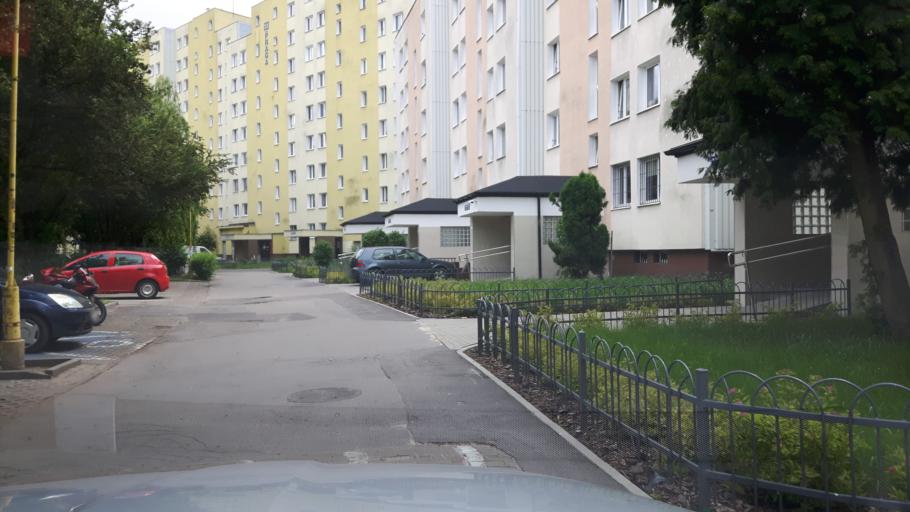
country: PL
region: Masovian Voivodeship
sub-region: Warszawa
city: Praga Polnoc
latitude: 52.2674
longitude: 21.0531
